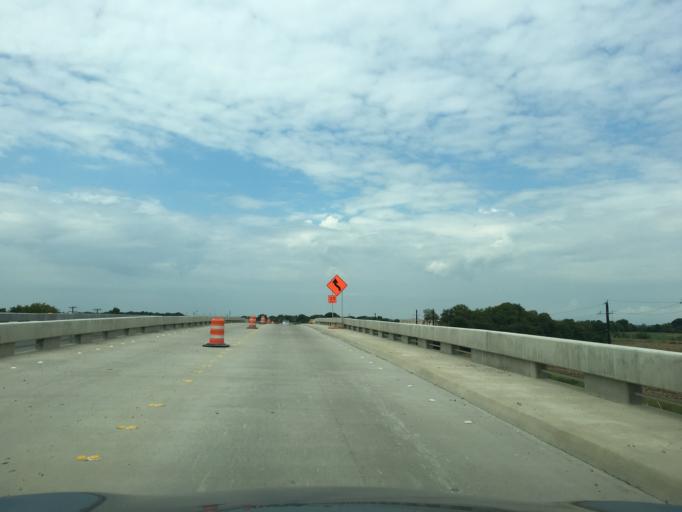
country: US
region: Texas
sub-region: Collin County
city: Melissa
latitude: 33.2752
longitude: -96.5757
